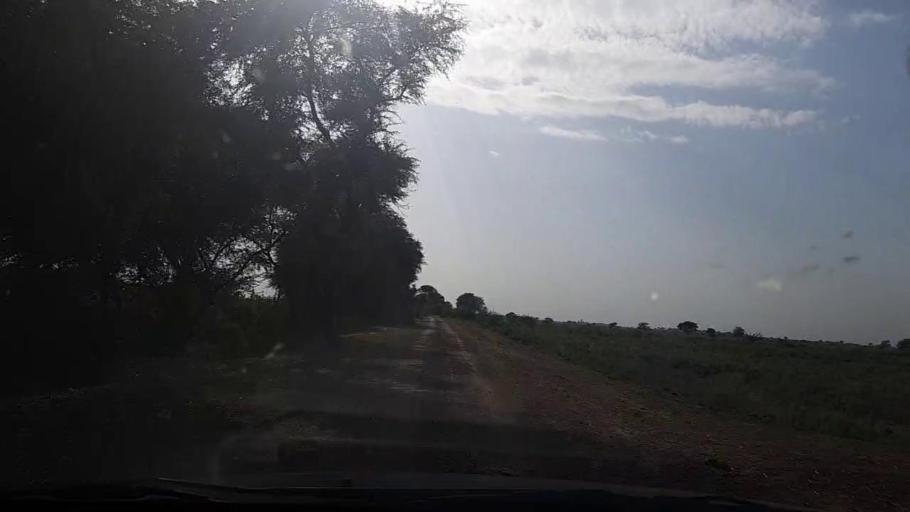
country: PK
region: Sindh
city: Mirpur Batoro
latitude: 24.5572
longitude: 68.1924
